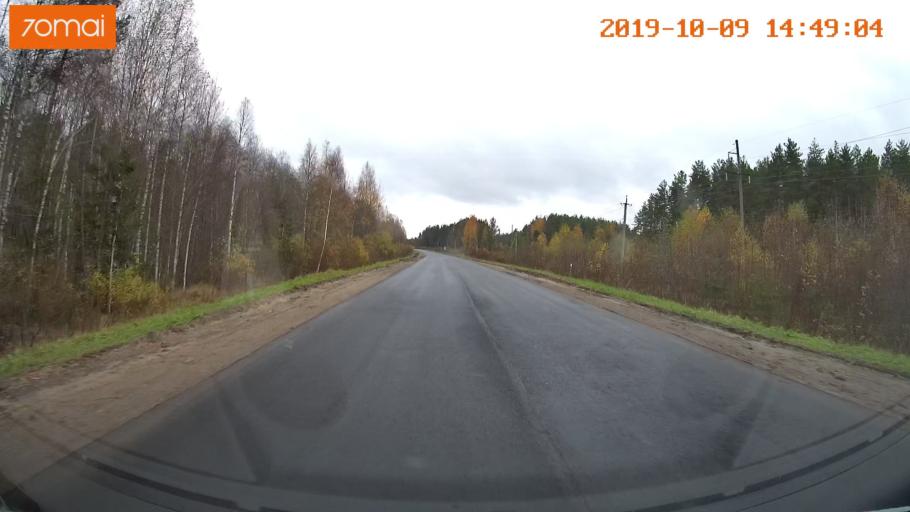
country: RU
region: Kostroma
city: Chistyye Bory
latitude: 58.3980
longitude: 41.5788
